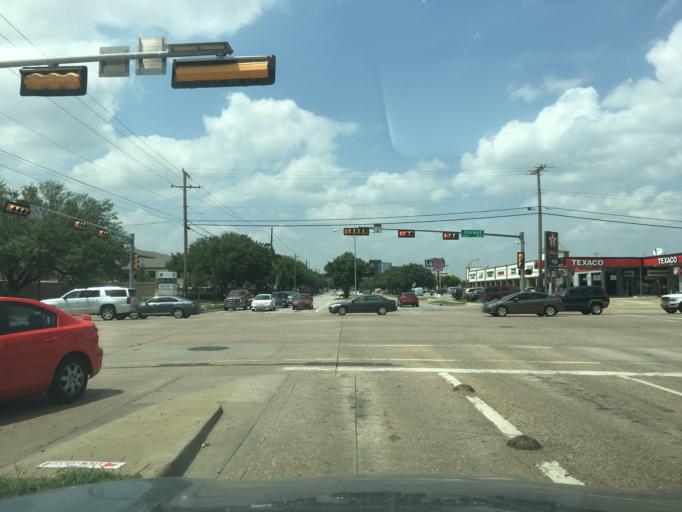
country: US
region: Texas
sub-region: Dallas County
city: Addison
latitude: 32.9087
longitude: -96.8184
